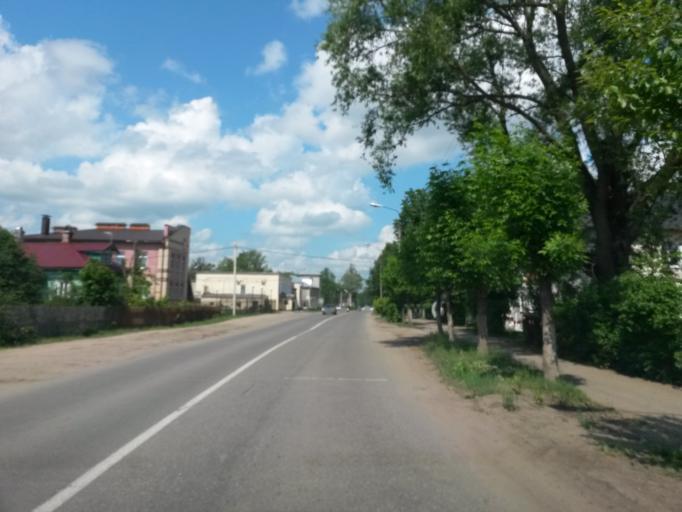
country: RU
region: Jaroslavl
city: Gavrilov-Yam
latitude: 57.3015
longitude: 39.8558
